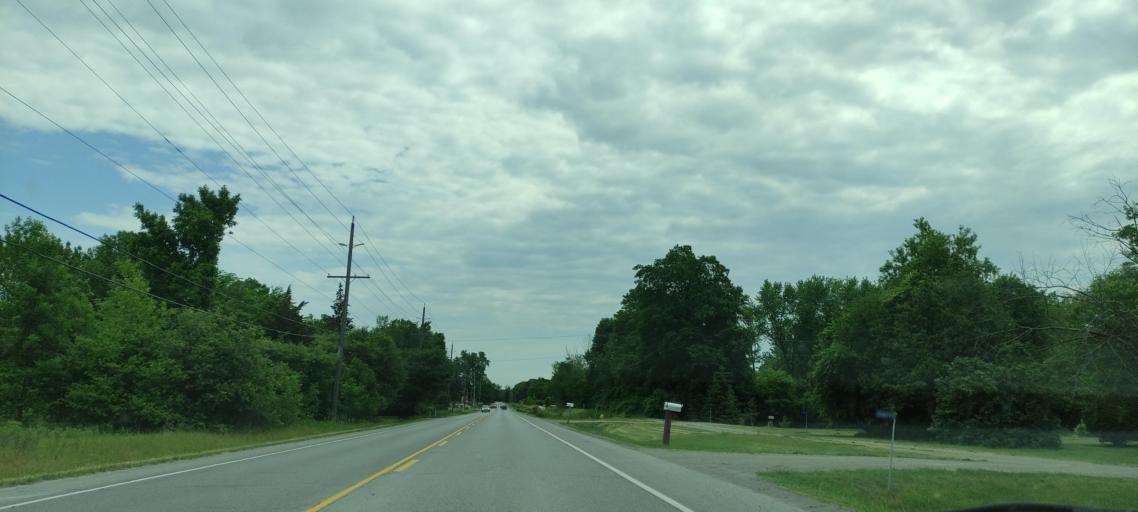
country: CA
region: Ontario
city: Quinte West
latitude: 44.0731
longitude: -77.5968
